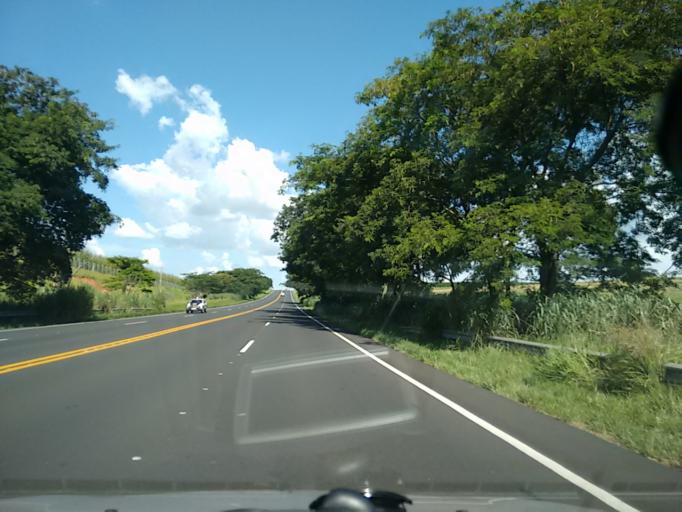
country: BR
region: Sao Paulo
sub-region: Pompeia
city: Pompeia
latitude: -22.1389
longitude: -50.1179
